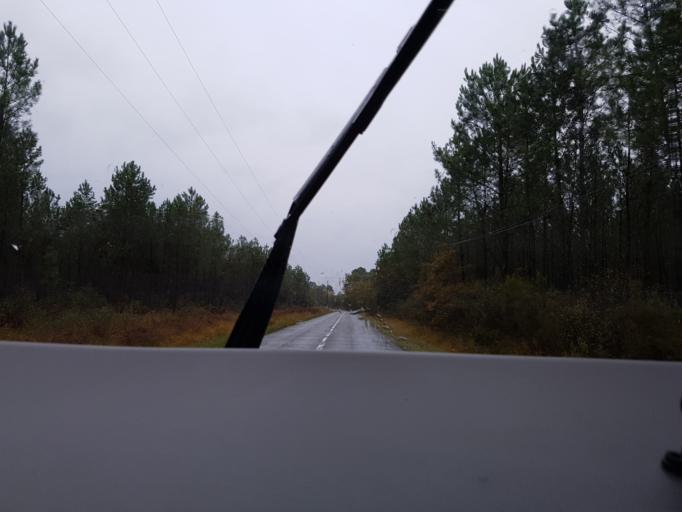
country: FR
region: Aquitaine
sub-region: Departement des Landes
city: Pissos
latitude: 44.3700
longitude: -0.6467
